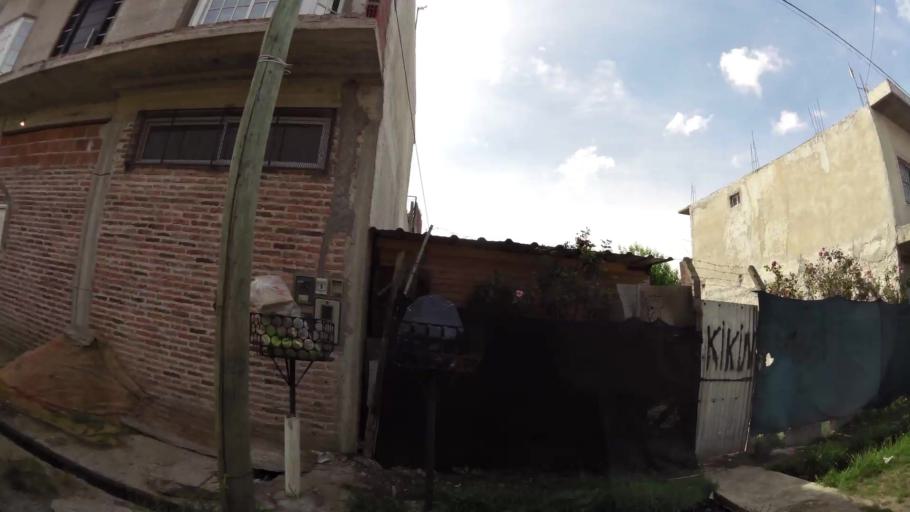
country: AR
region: Buenos Aires
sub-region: Partido de Quilmes
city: Quilmes
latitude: -34.7589
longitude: -58.2528
